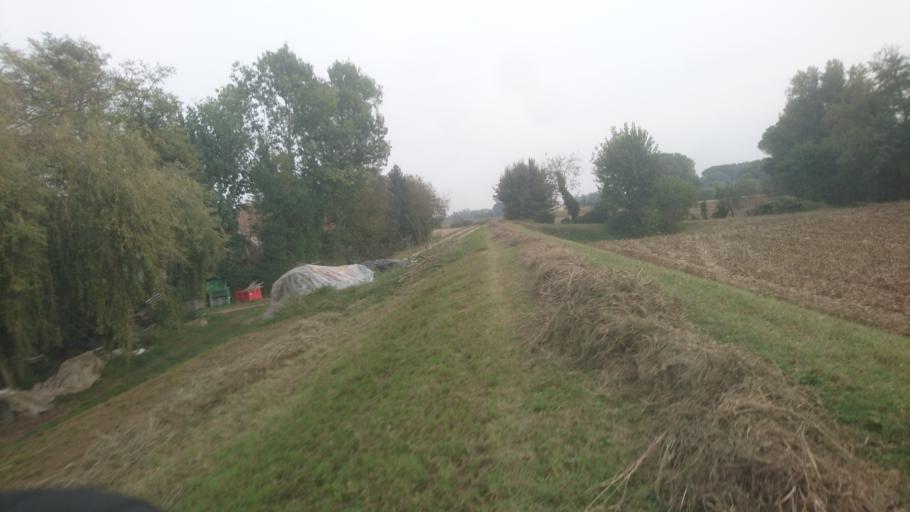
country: IT
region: Veneto
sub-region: Provincia di Padova
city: Cervarese Santa Croce
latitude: 45.4224
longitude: 11.7071
